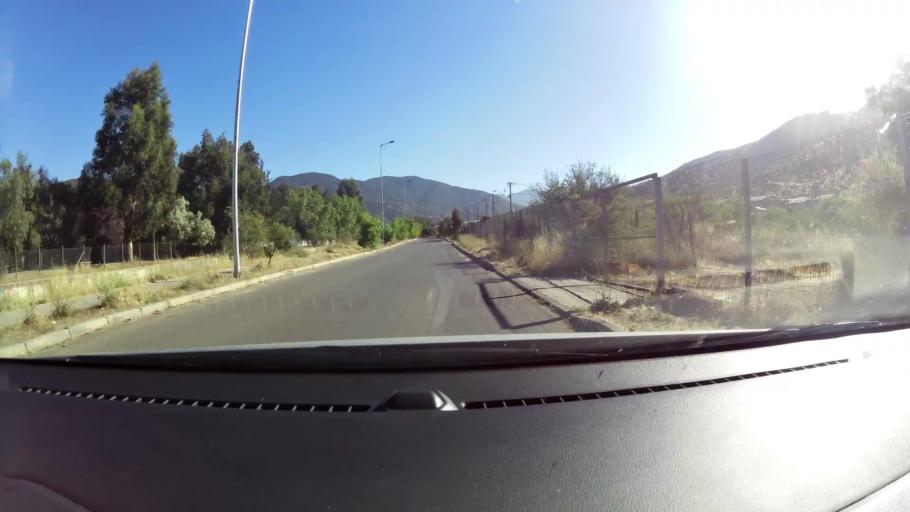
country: CL
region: Santiago Metropolitan
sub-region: Provincia de Chacabuco
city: Lampa
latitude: -33.3944
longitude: -71.1219
